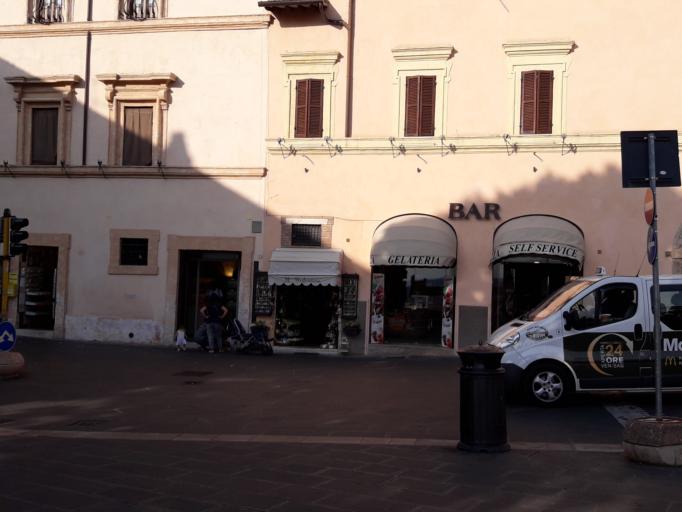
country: IT
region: Umbria
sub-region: Provincia di Perugia
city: Assisi
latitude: 43.0694
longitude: 12.6167
